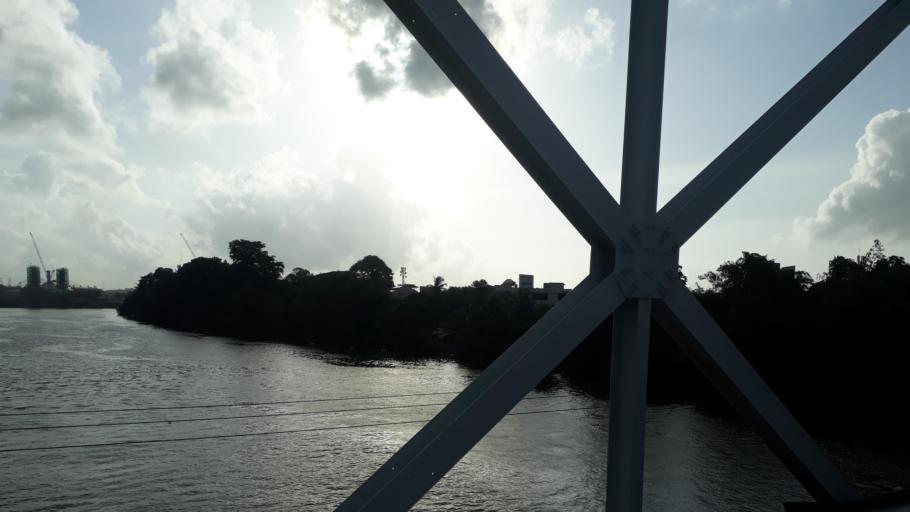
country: LK
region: Western
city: Peliyagoda
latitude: 6.9545
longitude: 79.8895
